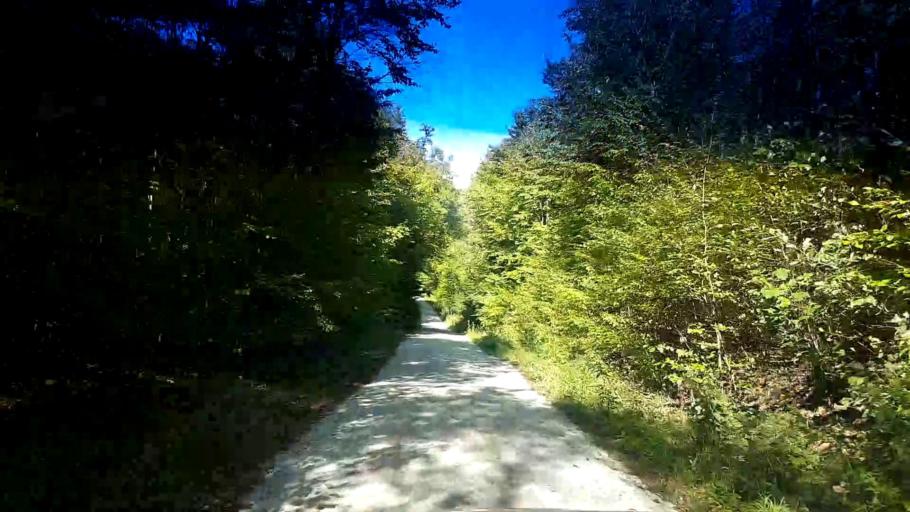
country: DE
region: Bavaria
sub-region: Upper Franconia
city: Litzendorf
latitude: 49.8884
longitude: 11.0177
